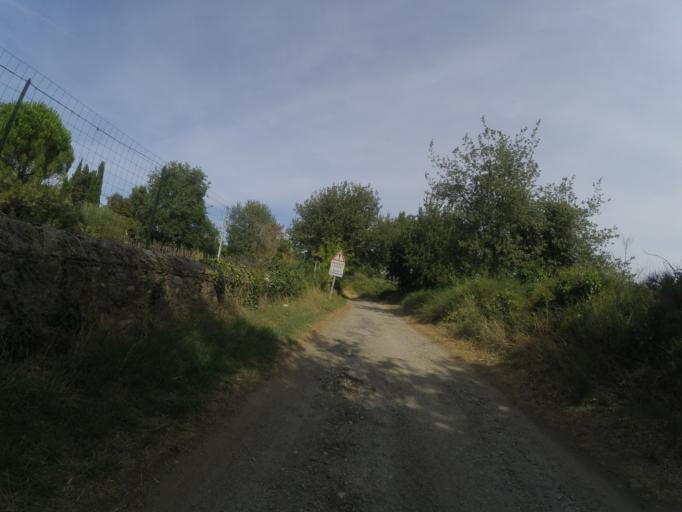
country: FR
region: Languedoc-Roussillon
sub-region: Departement des Pyrenees-Orientales
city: Ille-sur-Tet
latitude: 42.6624
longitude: 2.6256
